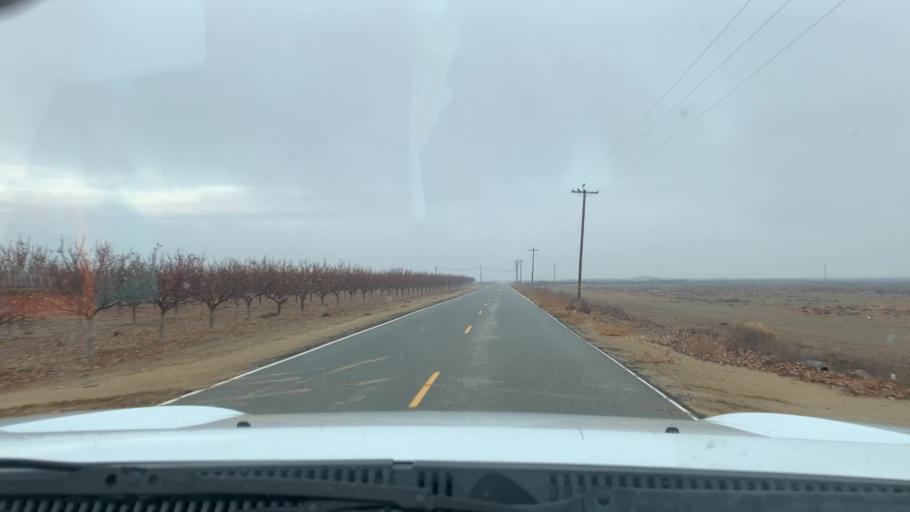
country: US
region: California
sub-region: Kern County
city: Lost Hills
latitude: 35.6338
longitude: -119.5800
